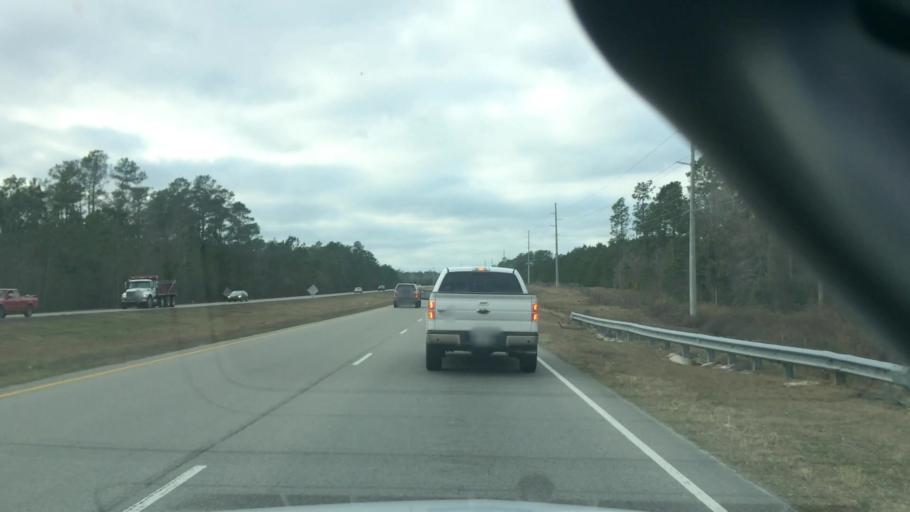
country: US
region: North Carolina
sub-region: Brunswick County
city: Shallotte
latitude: 33.9886
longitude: -78.3768
